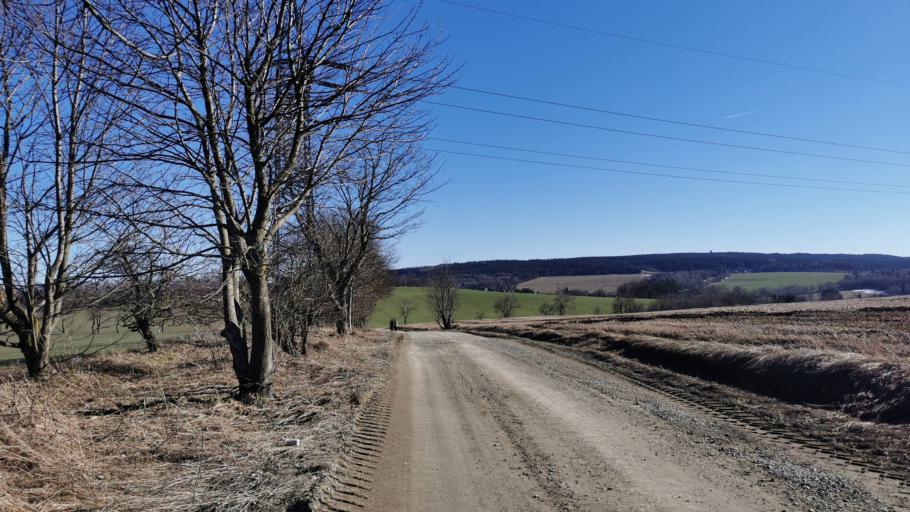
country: DE
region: Bavaria
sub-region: Upper Franconia
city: Ludwigsstadt
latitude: 50.4840
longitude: 11.4416
